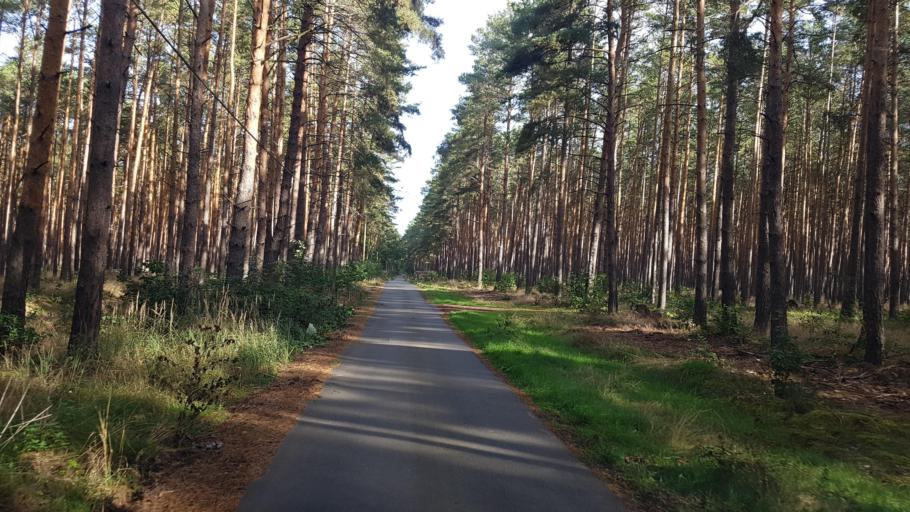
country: DE
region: Brandenburg
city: Hohenbucko
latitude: 51.8266
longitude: 13.5310
